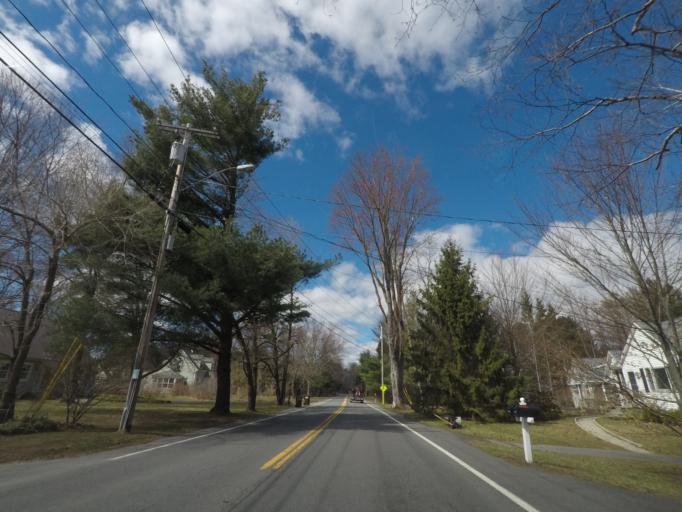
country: US
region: New York
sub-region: Albany County
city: Delmar
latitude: 42.5984
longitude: -73.8351
